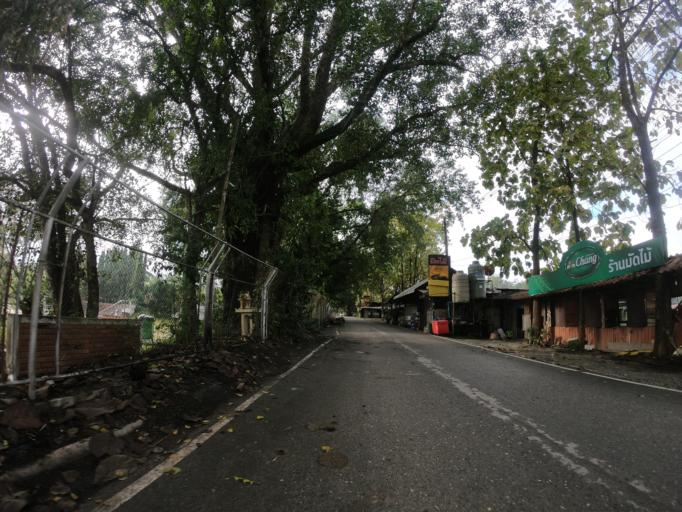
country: TH
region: Chiang Mai
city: Chiang Mai
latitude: 18.8215
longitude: 98.9767
